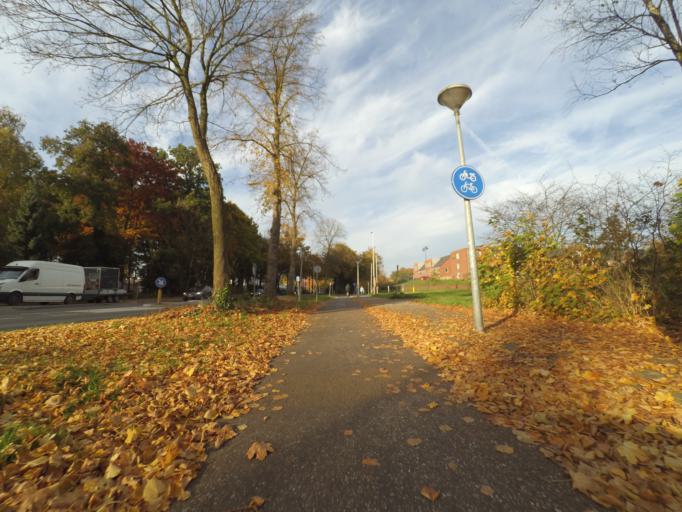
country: NL
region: Gelderland
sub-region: Gemeente Ede
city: Ede
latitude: 52.0227
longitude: 5.6719
